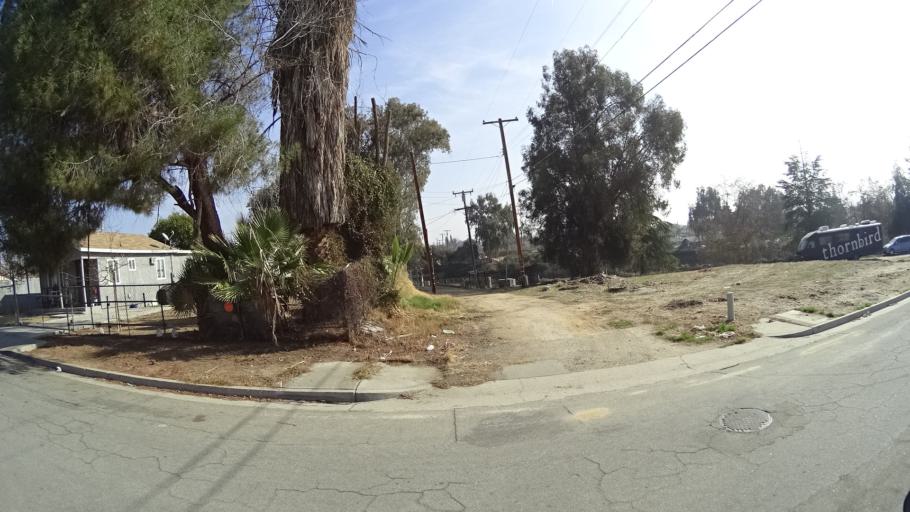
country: US
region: California
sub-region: Kern County
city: Bakersfield
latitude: 35.3889
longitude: -118.9835
